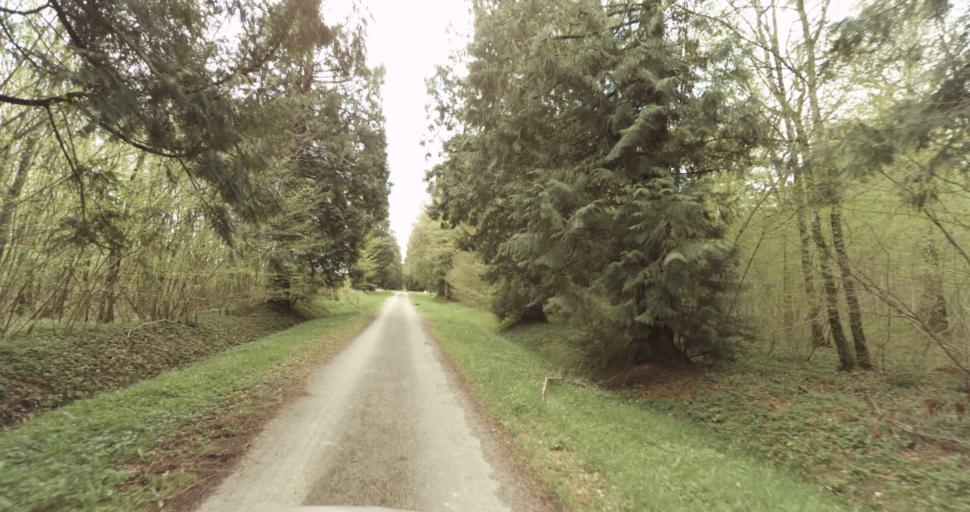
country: FR
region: Bourgogne
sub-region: Departement de la Cote-d'Or
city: Auxonne
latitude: 47.1651
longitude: 5.4233
